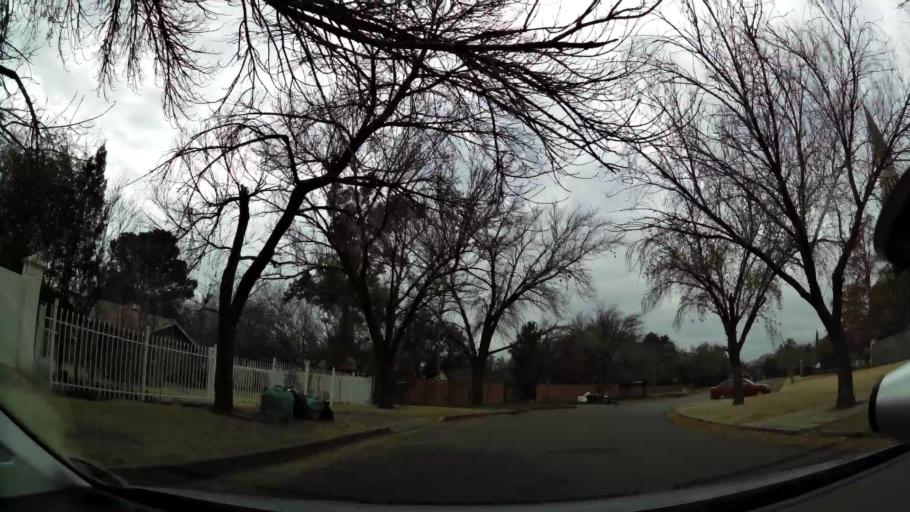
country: ZA
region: Orange Free State
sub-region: Fezile Dabi District Municipality
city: Kroonstad
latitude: -27.6724
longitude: 27.2491
